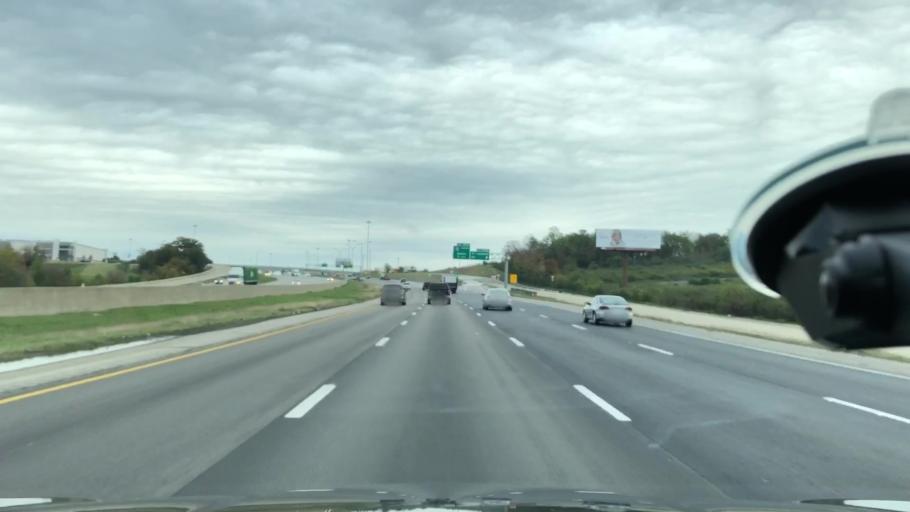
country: US
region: Texas
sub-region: Dallas County
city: Hutchins
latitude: 32.6575
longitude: -96.7373
